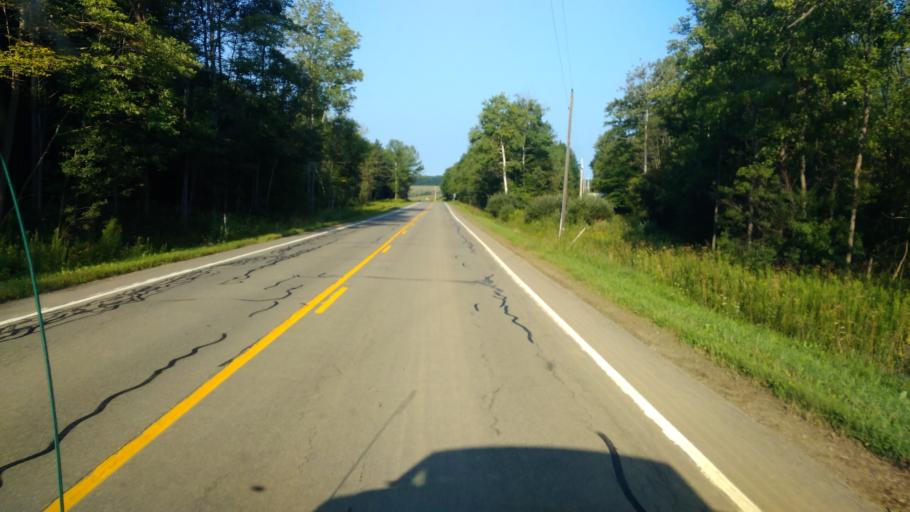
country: US
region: New York
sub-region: Allegany County
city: Andover
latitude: 42.1538
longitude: -77.7083
